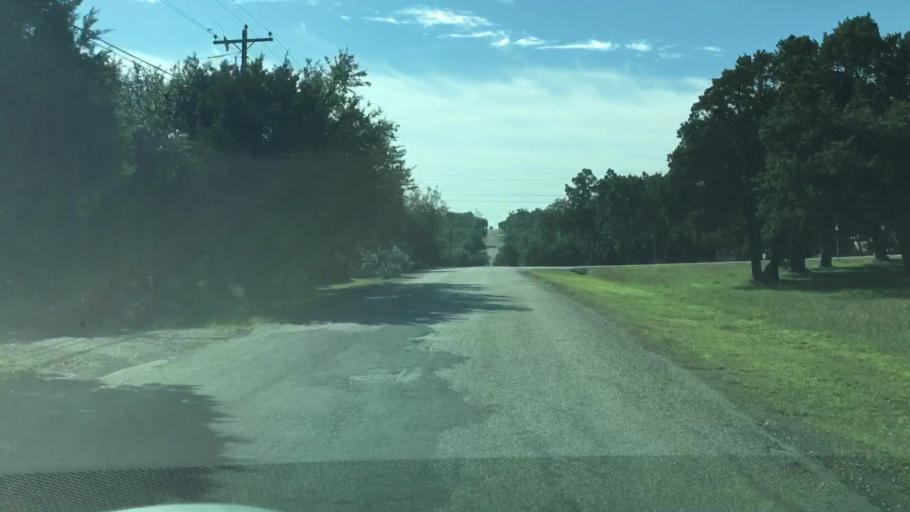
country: US
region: Texas
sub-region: Hays County
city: Dripping Springs
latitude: 30.1952
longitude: -98.0194
